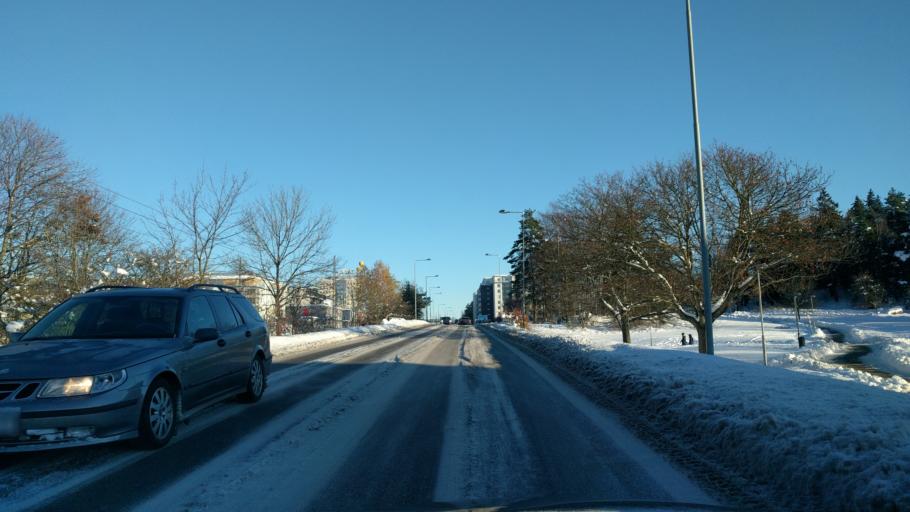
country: SE
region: Stockholm
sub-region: Taby Kommun
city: Taby
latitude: 59.4404
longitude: 18.0667
